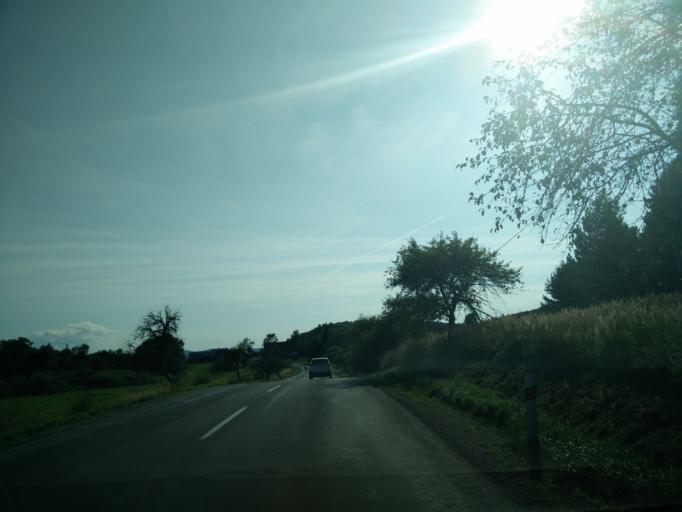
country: SK
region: Zilinsky
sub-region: Okres Martin
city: Martin
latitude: 48.9460
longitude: 18.8335
